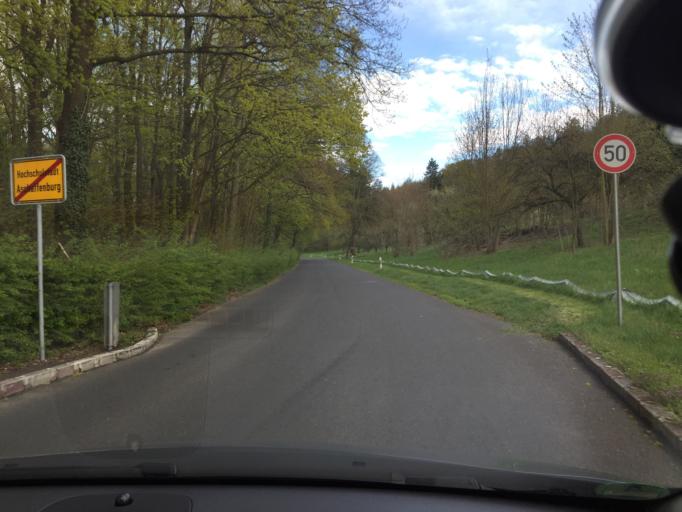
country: DE
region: Bavaria
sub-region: Regierungsbezirk Unterfranken
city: Goldbach
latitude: 49.9793
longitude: 9.1749
